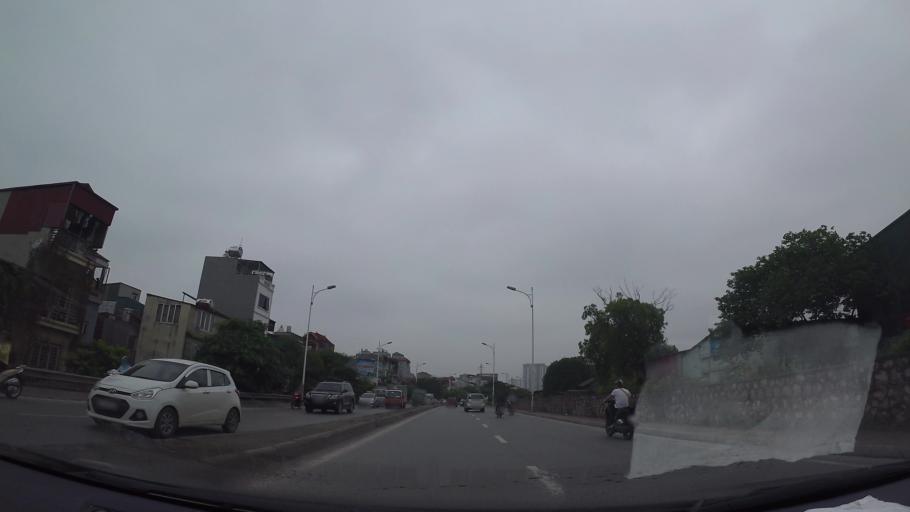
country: VN
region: Ha Noi
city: Hai BaTrung
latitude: 21.0035
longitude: 105.8712
